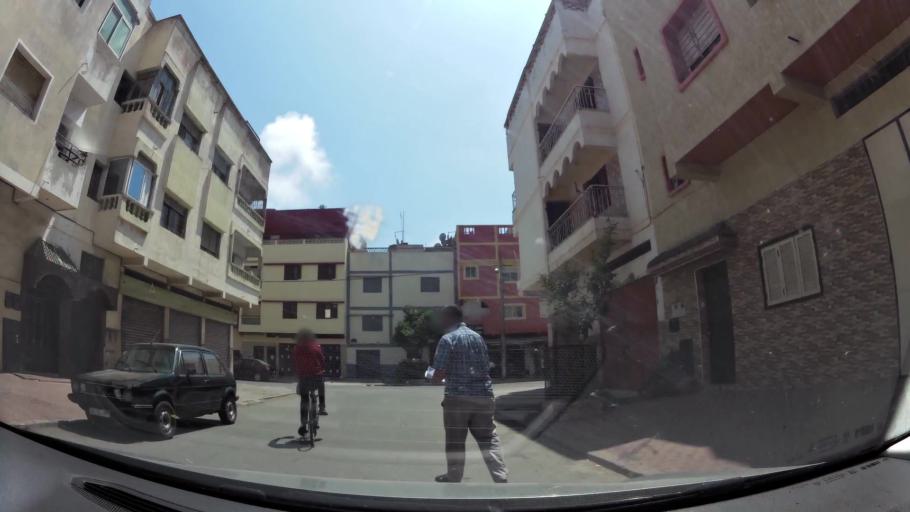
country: MA
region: Rabat-Sale-Zemmour-Zaer
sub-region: Skhirate-Temara
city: Temara
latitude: 33.9728
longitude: -6.8862
